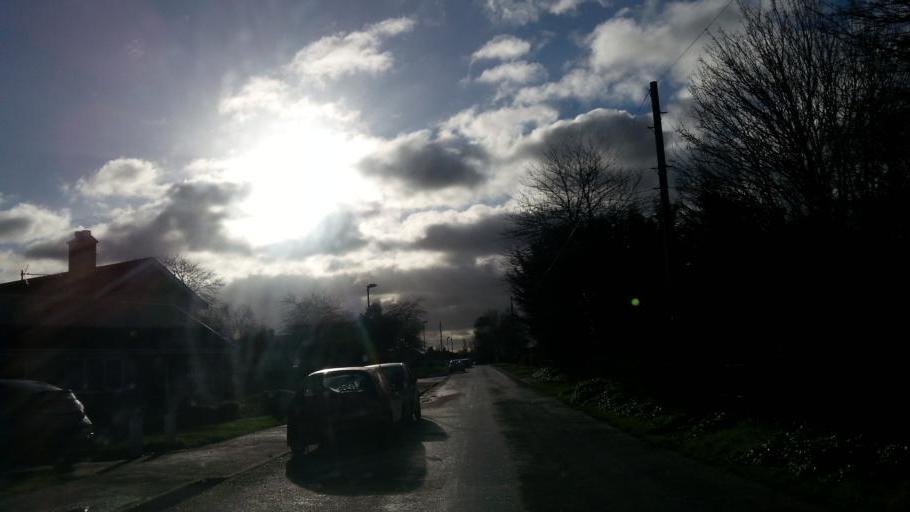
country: GB
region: England
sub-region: Norfolk
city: Ditchingham
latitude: 52.4706
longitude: 1.4442
